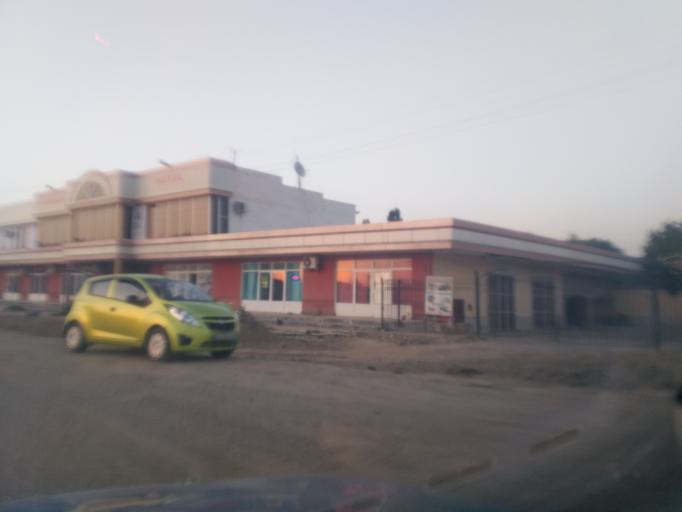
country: UZ
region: Sirdaryo
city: Guliston
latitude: 40.5042
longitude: 68.7685
